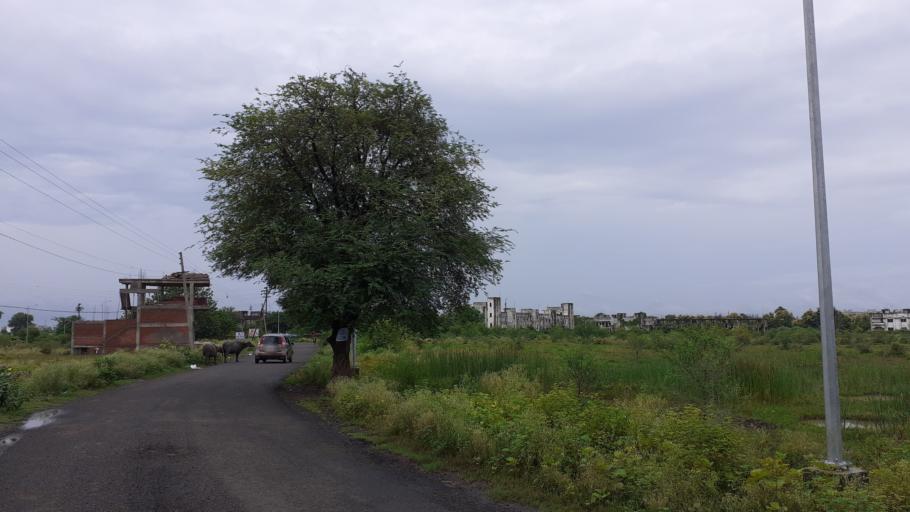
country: IN
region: Maharashtra
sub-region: Nagpur Division
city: Nagpur
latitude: 21.0828
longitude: 79.1116
